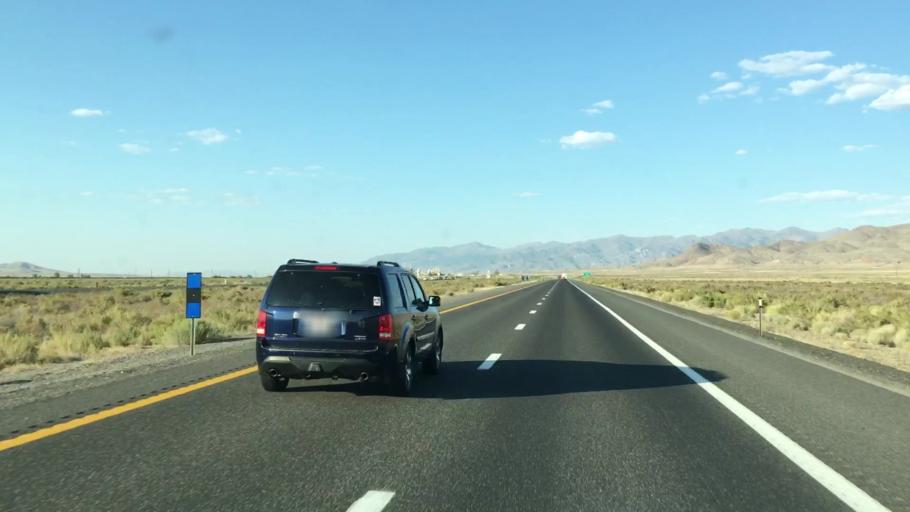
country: US
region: Nevada
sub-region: Pershing County
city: Lovelock
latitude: 40.2278
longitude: -118.4006
